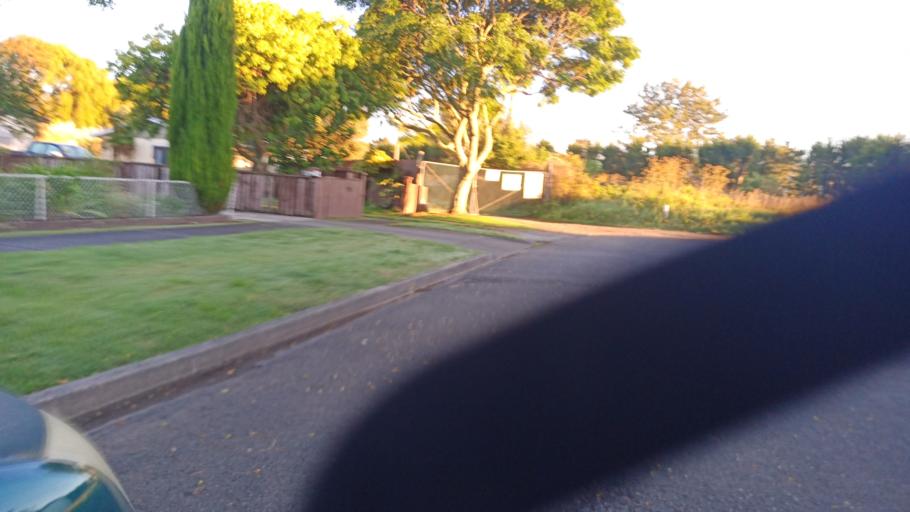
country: NZ
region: Gisborne
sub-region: Gisborne District
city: Gisborne
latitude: -38.6572
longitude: 177.9858
